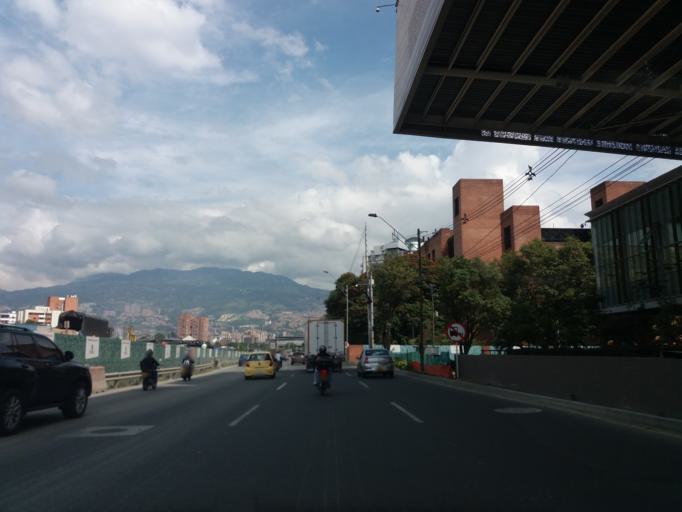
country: CO
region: Antioquia
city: Medellin
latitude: 6.2417
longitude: -75.5775
